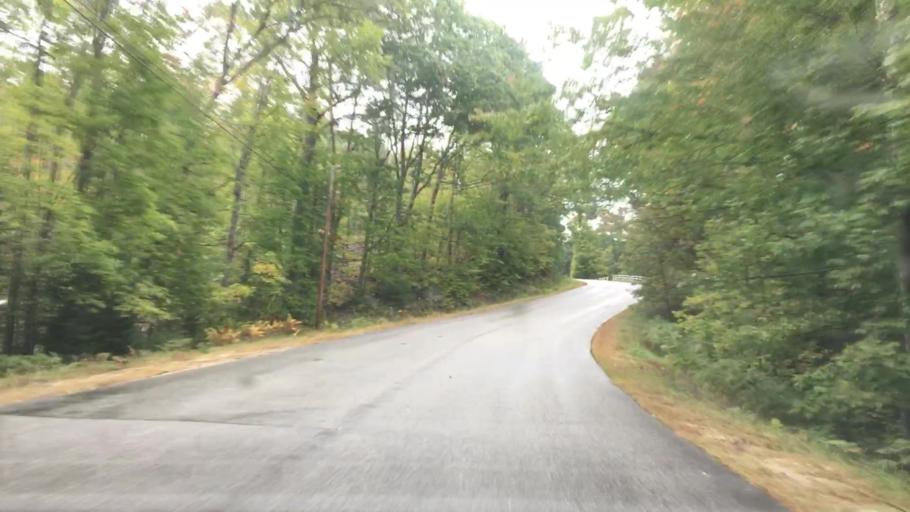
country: US
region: Maine
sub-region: Cumberland County
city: Harrison
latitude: 44.0523
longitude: -70.6181
